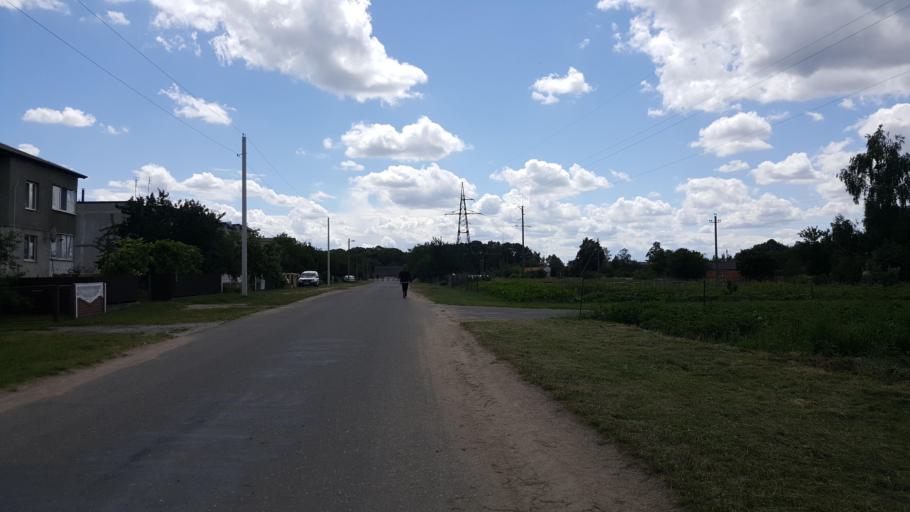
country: BY
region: Brest
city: Kamyanyets
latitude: 52.3202
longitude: 23.9242
